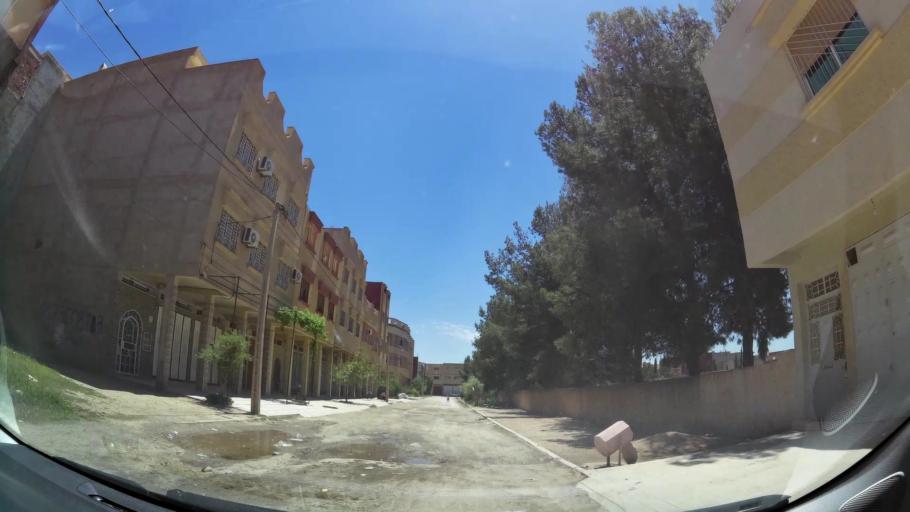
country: MA
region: Oriental
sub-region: Oujda-Angad
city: Oujda
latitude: 34.6774
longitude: -1.8728
